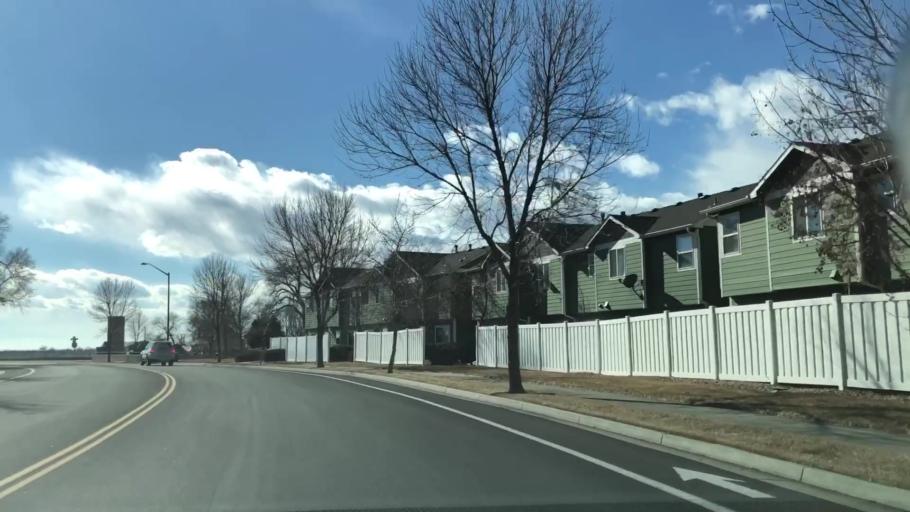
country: US
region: Colorado
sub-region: Larimer County
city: Fort Collins
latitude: 40.5970
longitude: -105.0053
